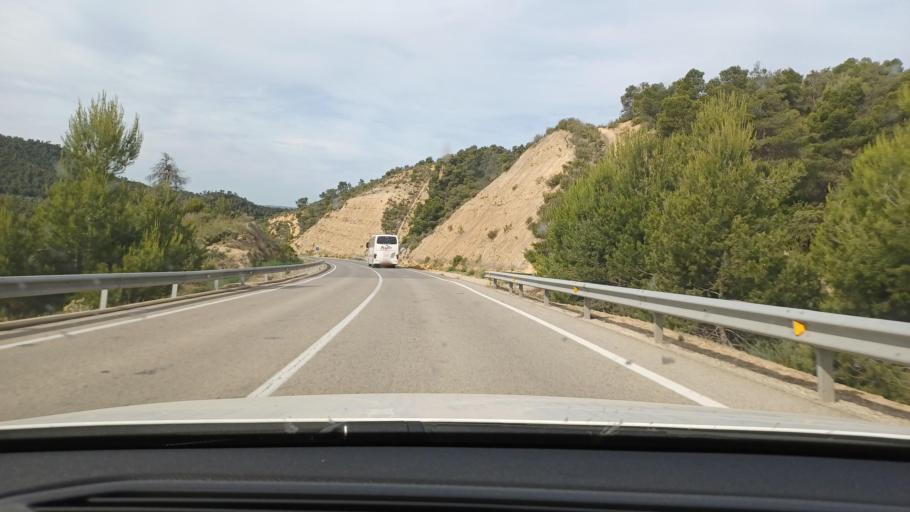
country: ES
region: Catalonia
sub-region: Provincia de Tarragona
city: Batea
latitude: 41.1100
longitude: 0.2474
